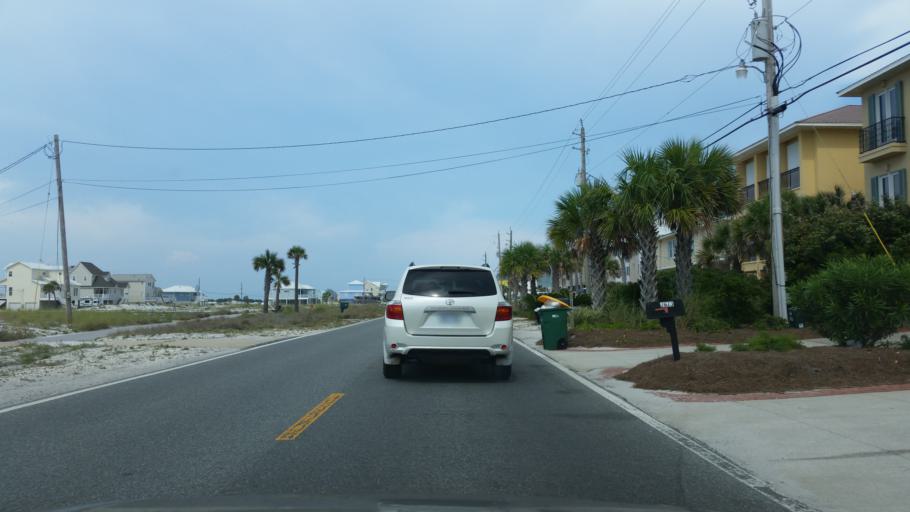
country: US
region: Florida
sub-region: Santa Rosa County
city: Navarre
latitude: 30.3743
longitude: -86.9026
